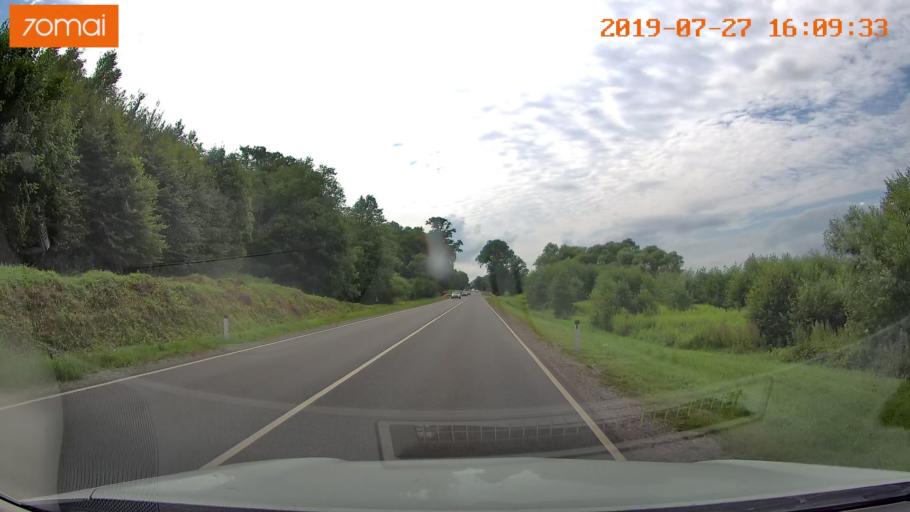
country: RU
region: Kaliningrad
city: Chernyakhovsk
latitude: 54.6384
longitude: 21.7126
